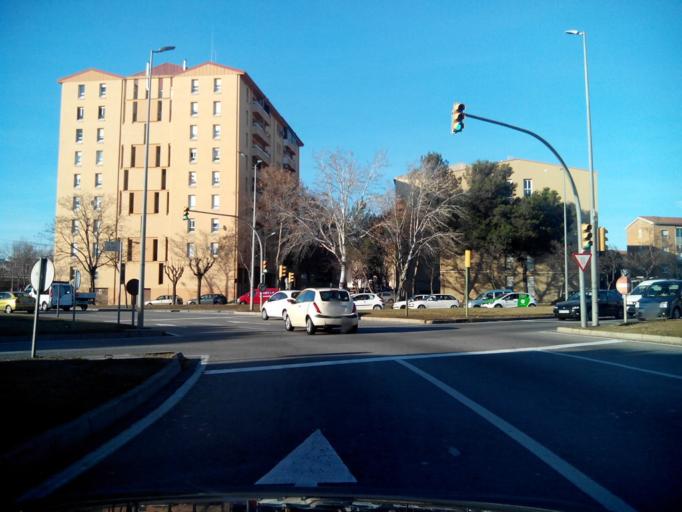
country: ES
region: Catalonia
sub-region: Provincia de Barcelona
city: Sant Quirze del Valles
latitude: 41.5379
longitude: 2.0965
